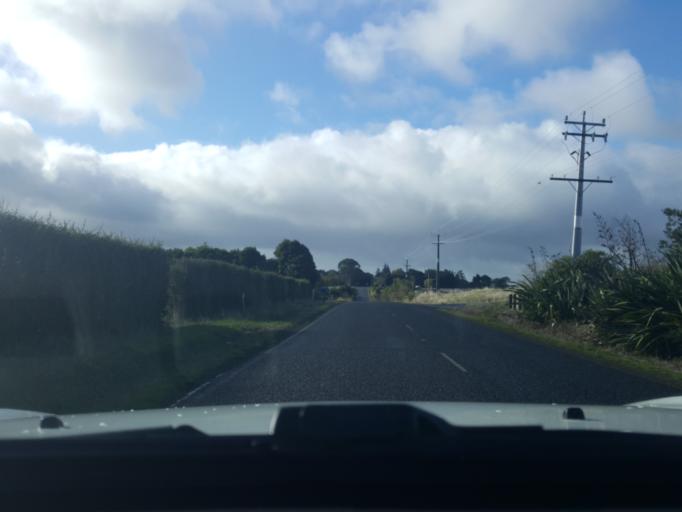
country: NZ
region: Auckland
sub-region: Auckland
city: Pukekohe East
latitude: -37.3086
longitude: 175.0027
